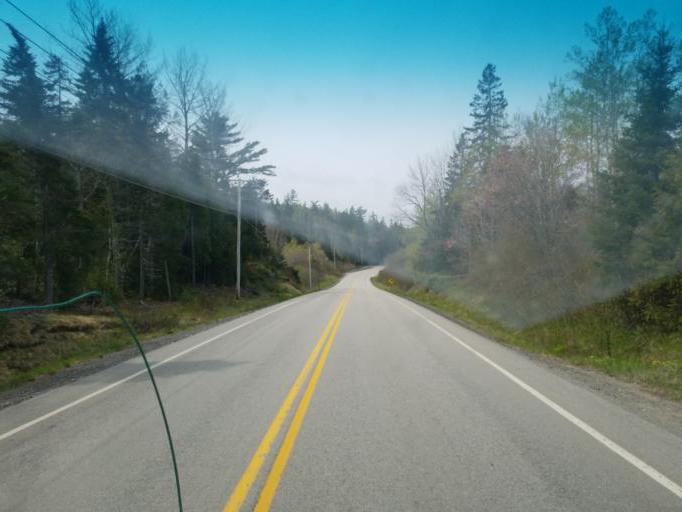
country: US
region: Maine
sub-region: Washington County
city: Eastport
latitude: 44.7981
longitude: -67.1448
